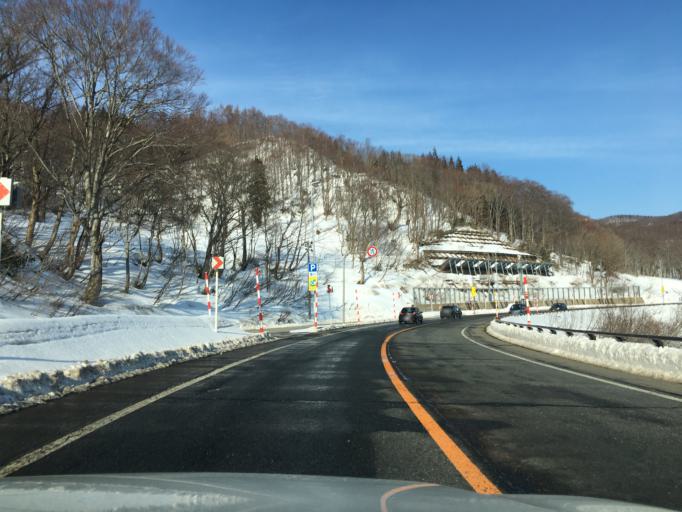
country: JP
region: Yamagata
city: Tsuruoka
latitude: 38.5806
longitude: 139.9368
